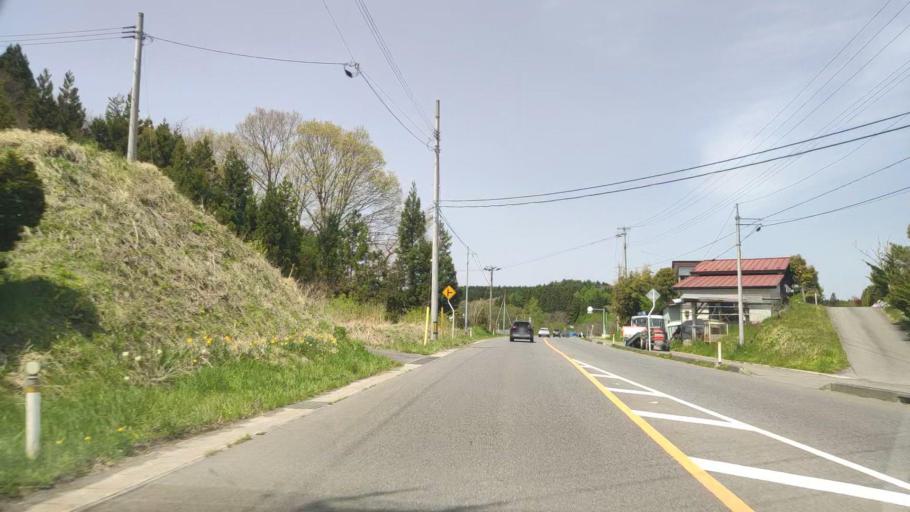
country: JP
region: Aomori
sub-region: Misawa Shi
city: Inuotose
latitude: 40.5612
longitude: 141.3837
